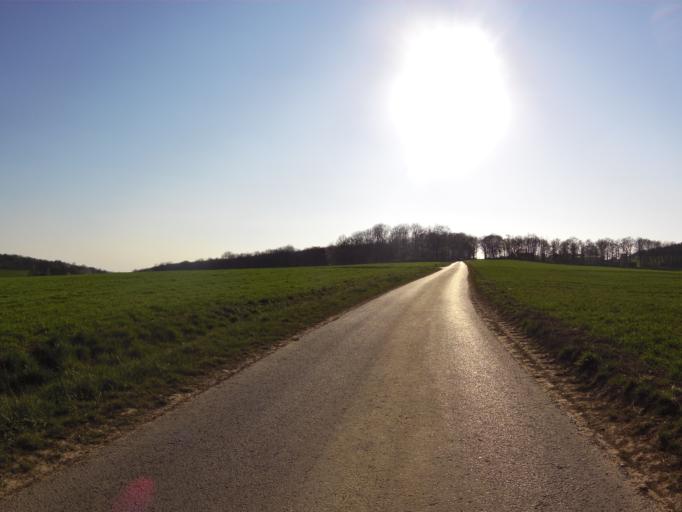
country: DE
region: Bavaria
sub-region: Regierungsbezirk Unterfranken
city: Rottendorf
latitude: 49.8241
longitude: 10.0714
